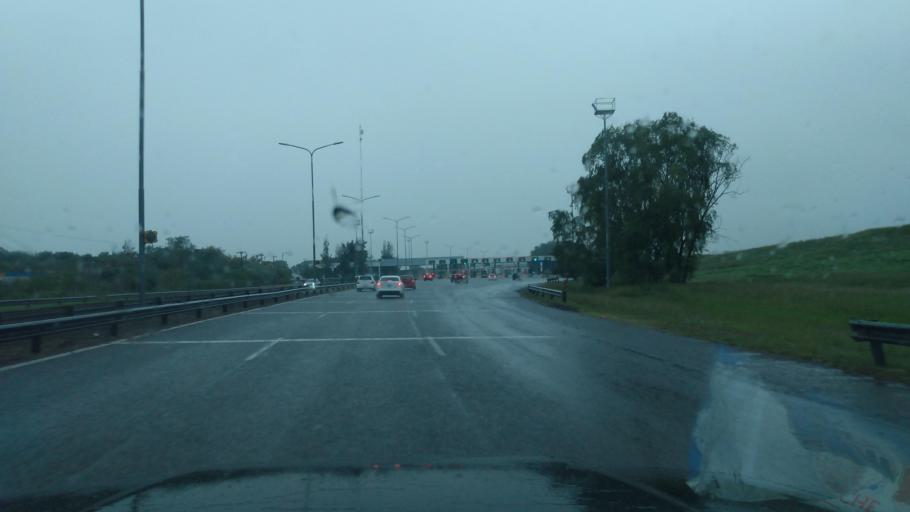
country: AR
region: Buenos Aires
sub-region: Partido de Tigre
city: Tigre
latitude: -34.5011
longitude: -58.5902
